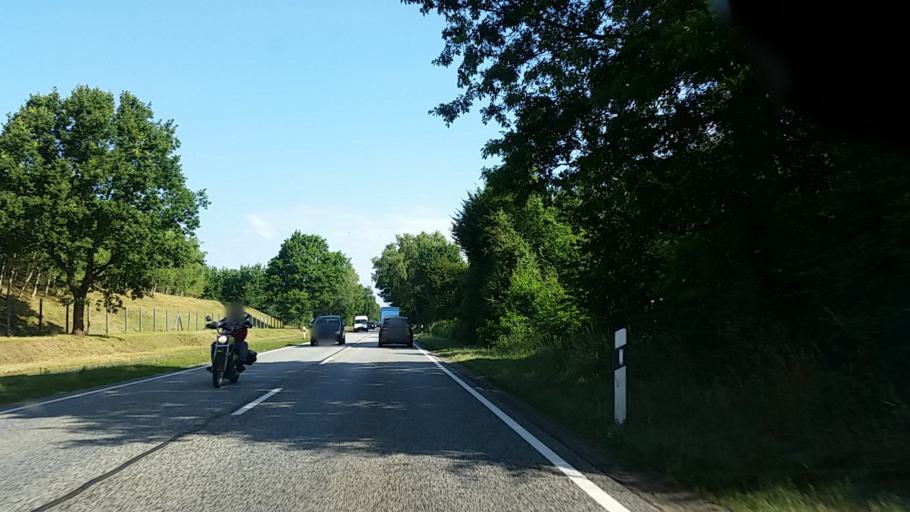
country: DE
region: Schleswig-Holstein
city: Tangstedt
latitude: 53.7163
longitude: 10.0290
